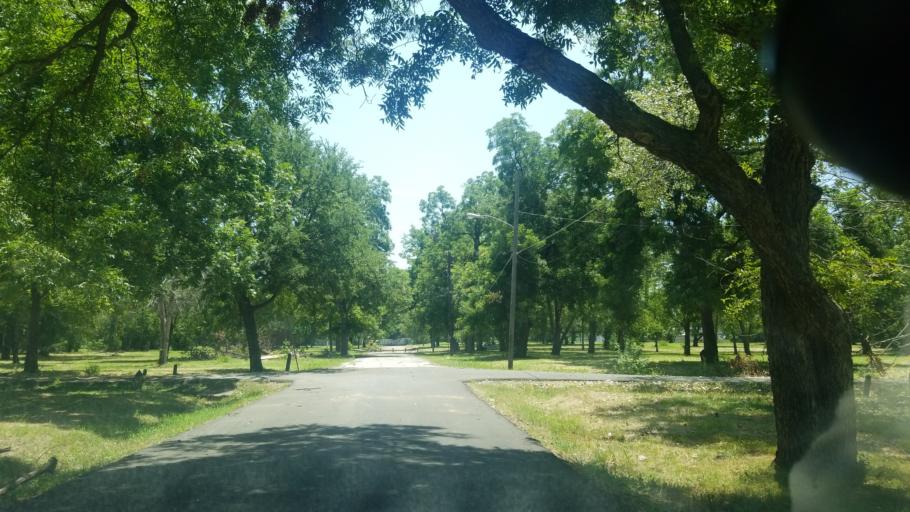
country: US
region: Texas
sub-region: Dallas County
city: Dallas
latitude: 32.7415
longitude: -96.7862
